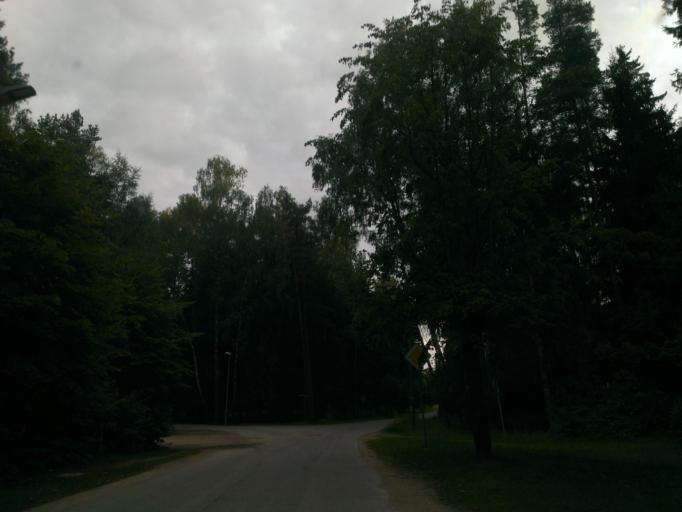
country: LV
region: Ogre
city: Ogre
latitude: 56.8257
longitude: 24.5827
